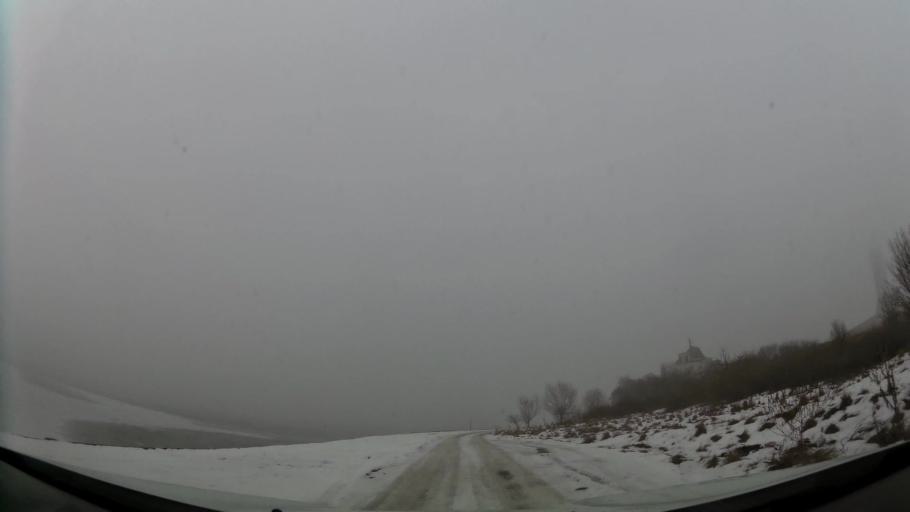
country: RO
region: Ilfov
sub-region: Comuna Chiajna
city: Rosu
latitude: 44.4465
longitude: 26.0345
